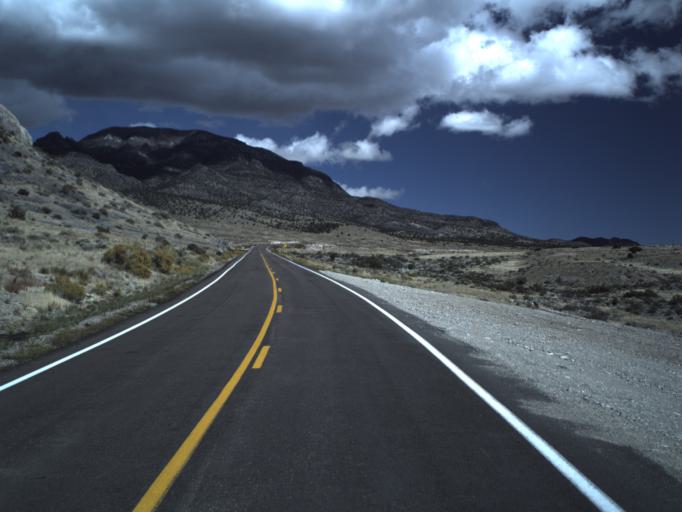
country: US
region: Utah
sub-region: Beaver County
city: Milford
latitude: 38.5073
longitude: -113.5904
